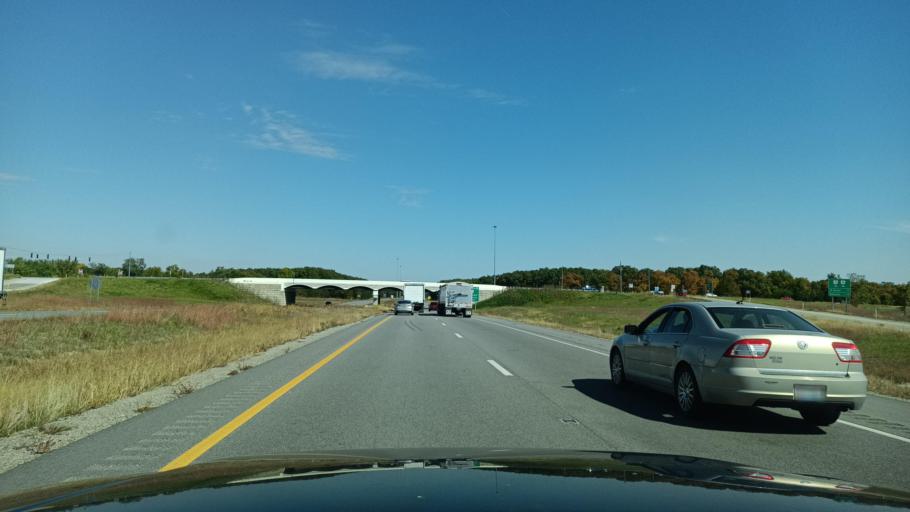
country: US
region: Ohio
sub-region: Defiance County
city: Defiance
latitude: 41.3003
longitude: -84.3788
